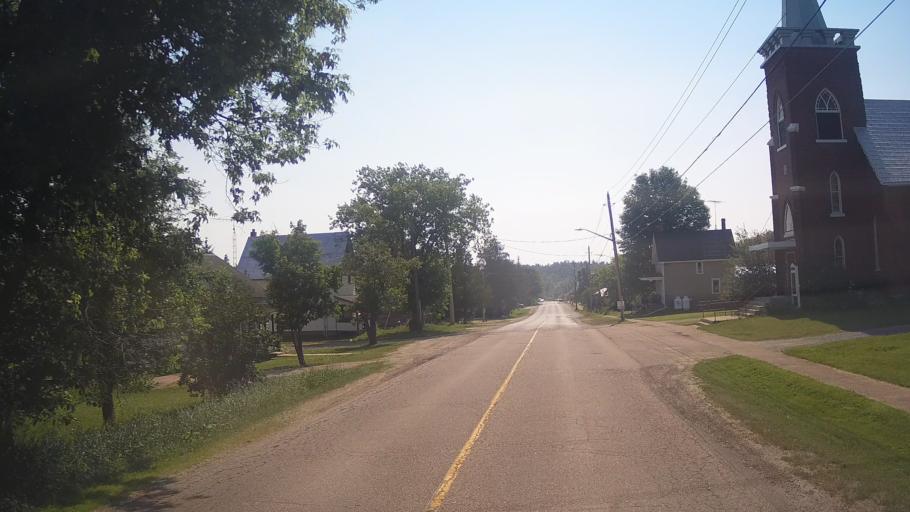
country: CA
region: Ontario
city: Pembroke
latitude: 45.5823
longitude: -77.2390
